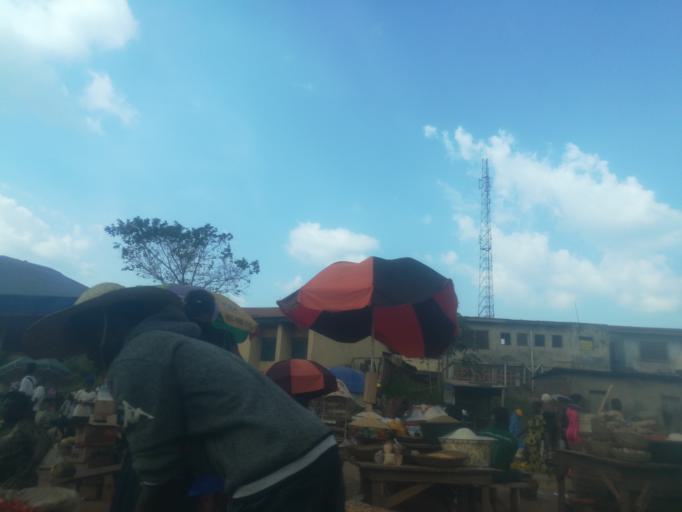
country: NG
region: Ogun
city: Abeokuta
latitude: 7.1815
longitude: 3.3469
